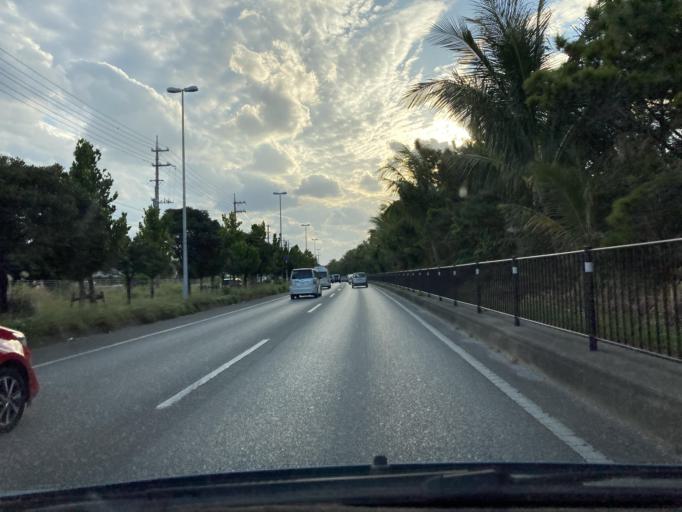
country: JP
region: Okinawa
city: Ginowan
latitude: 26.2849
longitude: 127.7463
